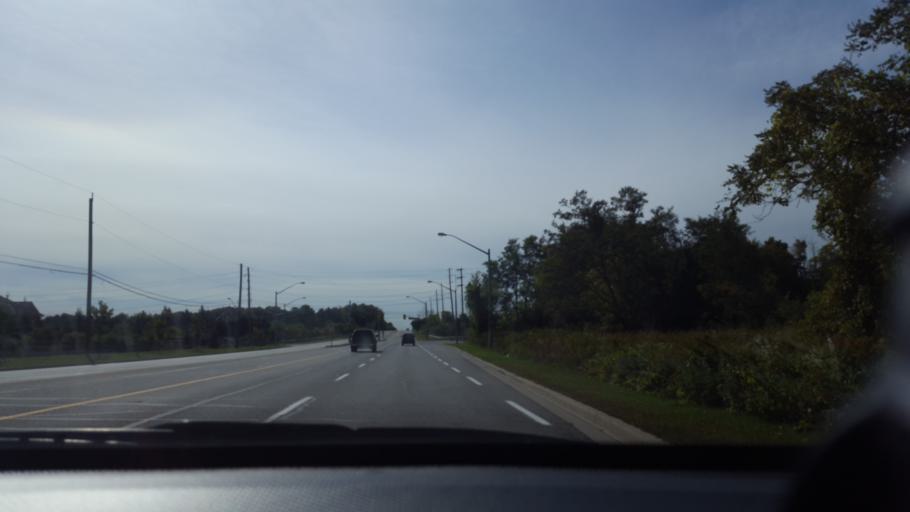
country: CA
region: Ontario
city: Newmarket
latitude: 44.0137
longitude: -79.4987
